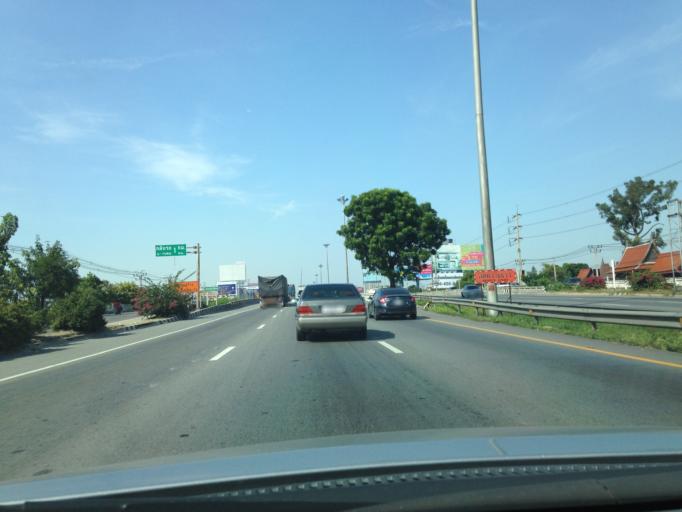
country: TH
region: Nonthaburi
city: Bang Yai
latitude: 13.8502
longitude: 100.4121
